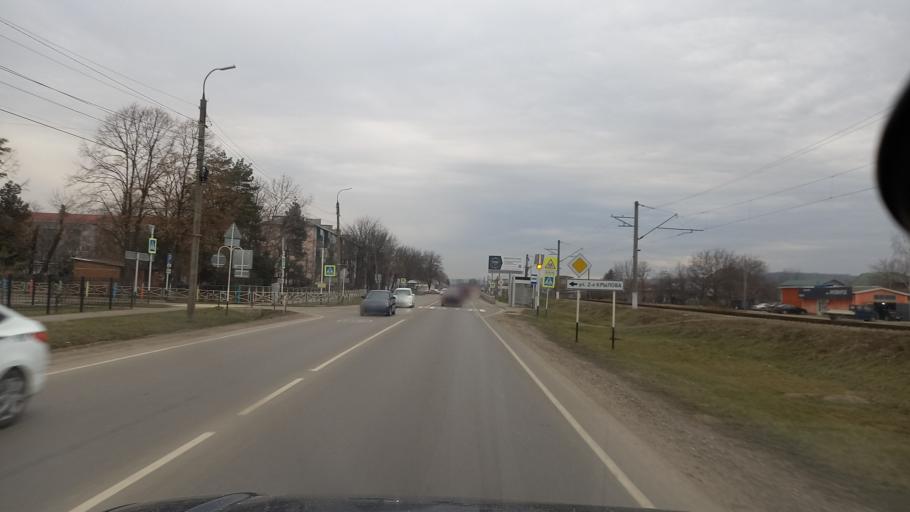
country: RU
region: Adygeya
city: Maykop
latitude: 44.5969
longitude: 40.1324
